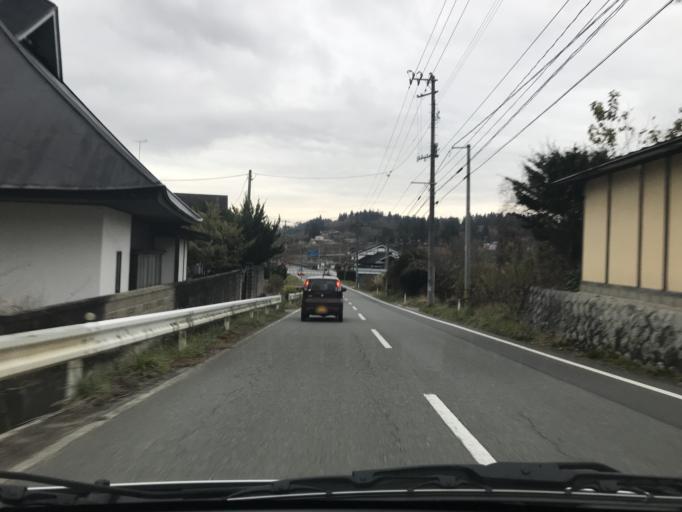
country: JP
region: Iwate
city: Ichinoseki
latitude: 39.0225
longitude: 141.3309
